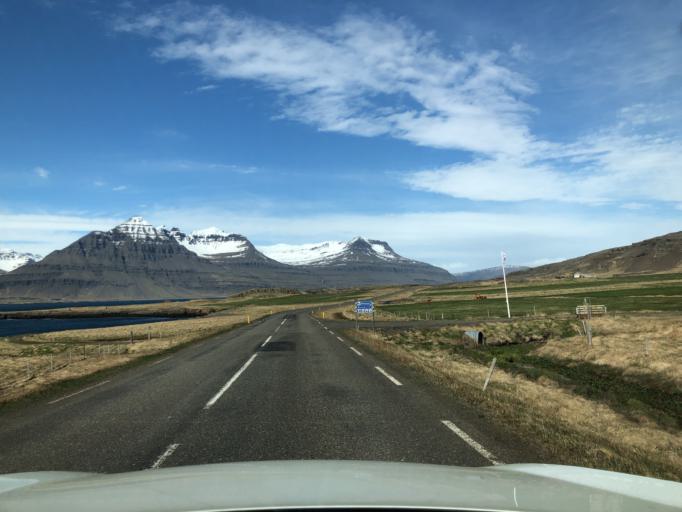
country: IS
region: East
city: Reydarfjoerdur
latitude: 64.6951
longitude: -14.2574
